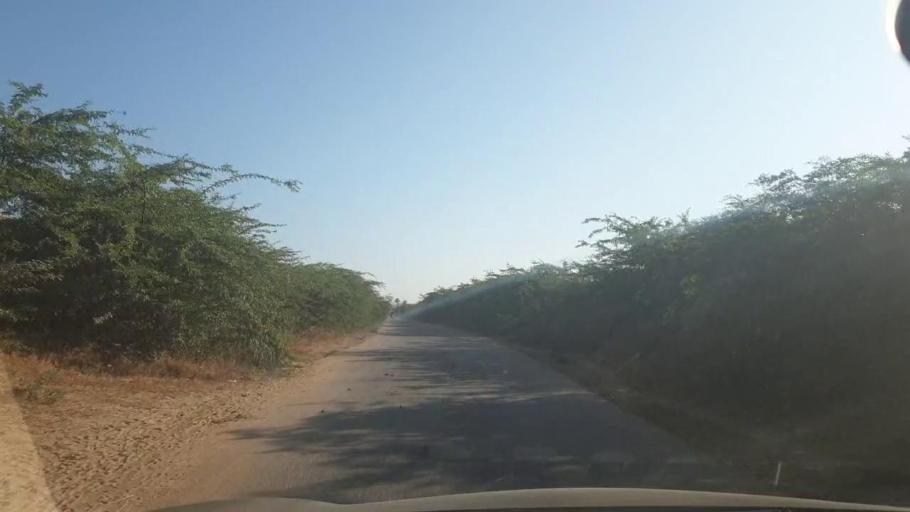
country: PK
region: Sindh
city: Malir Cantonment
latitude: 25.1144
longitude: 67.2724
